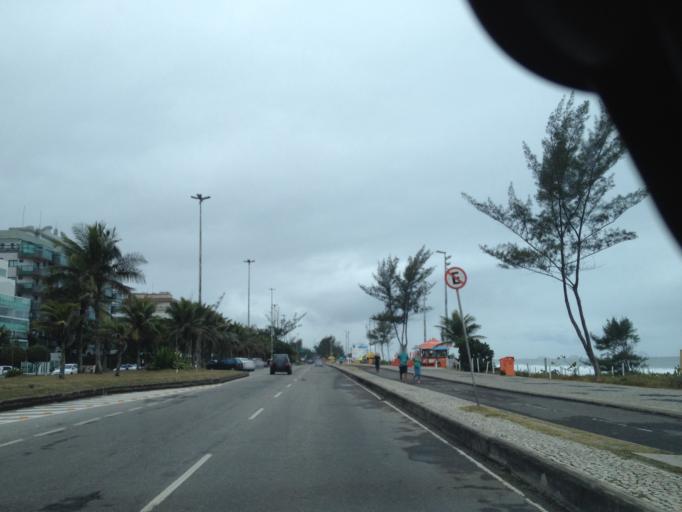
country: BR
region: Rio de Janeiro
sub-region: Nilopolis
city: Nilopolis
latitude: -23.0235
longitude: -43.4513
